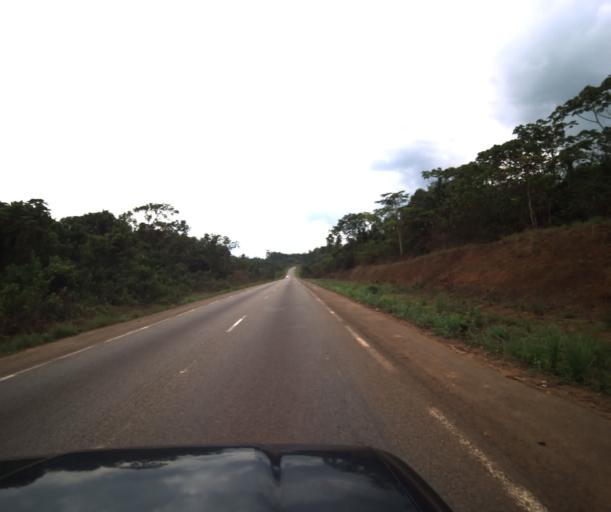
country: CM
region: Littoral
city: Edea
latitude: 3.8707
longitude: 10.0728
